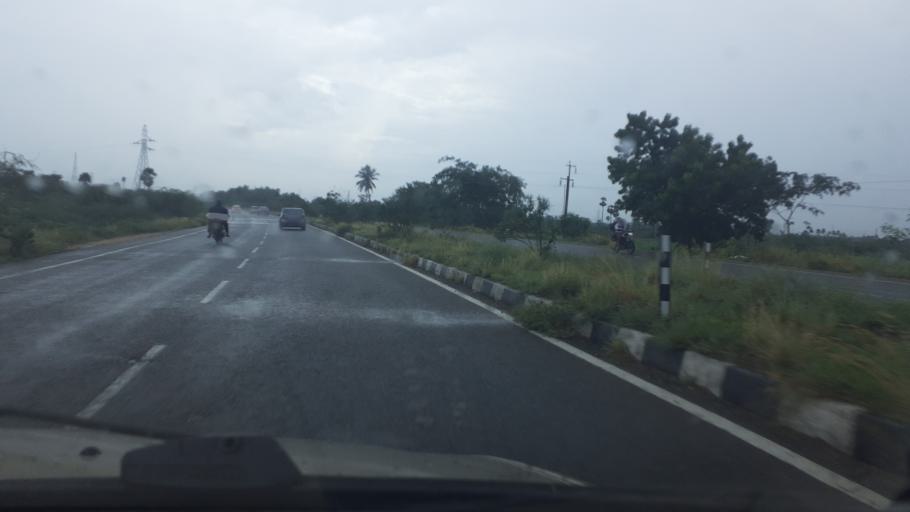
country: IN
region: Tamil Nadu
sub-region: Thoothukkudi
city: Kayattar
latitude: 8.9543
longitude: 77.7682
